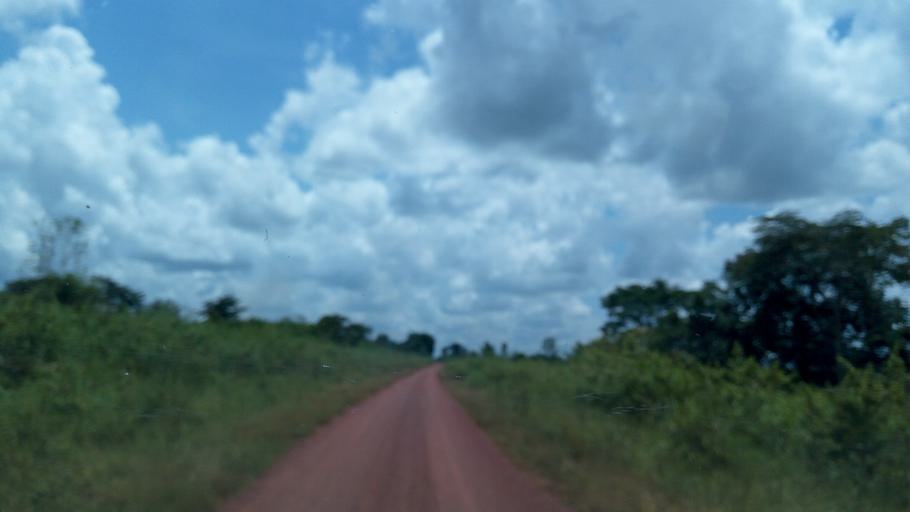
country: CD
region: Equateur
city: Libenge
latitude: 3.7727
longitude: 18.9439
